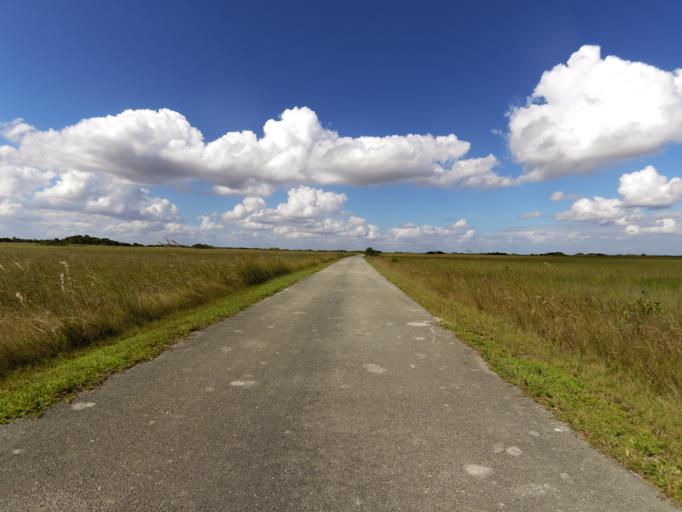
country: US
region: Florida
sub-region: Miami-Dade County
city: The Hammocks
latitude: 25.6763
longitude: -80.7627
